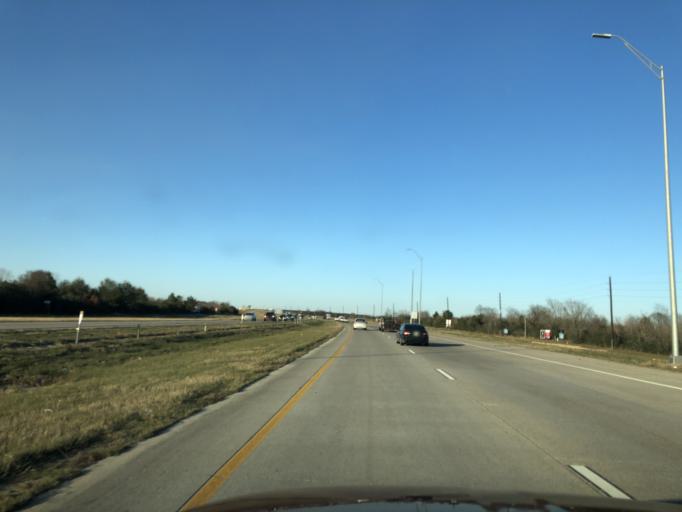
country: US
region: Texas
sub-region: Harris County
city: Katy
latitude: 29.8370
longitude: -95.7577
